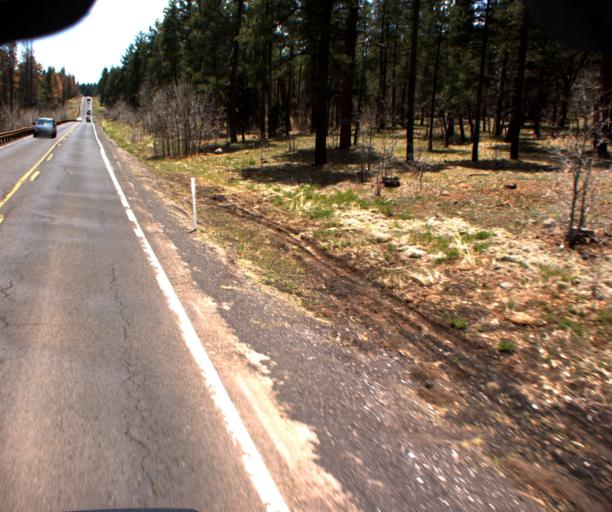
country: US
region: Arizona
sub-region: Coconino County
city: Kachina Village
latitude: 35.0526
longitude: -111.7328
